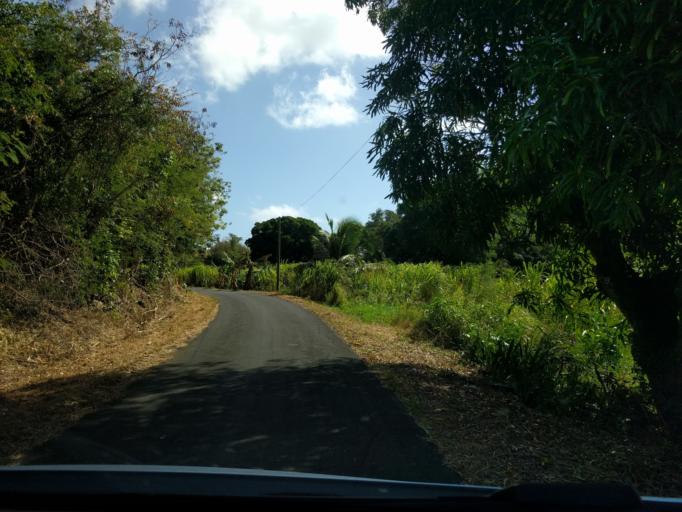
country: GP
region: Guadeloupe
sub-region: Guadeloupe
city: Grand-Bourg
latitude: 15.9746
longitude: -61.2582
